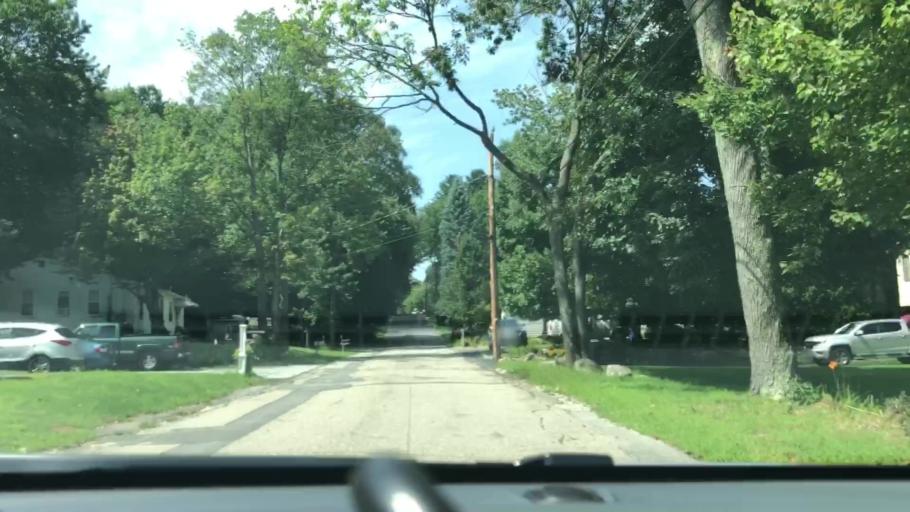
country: US
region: New Hampshire
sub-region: Hillsborough County
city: Pinardville
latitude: 42.9921
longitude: -71.5119
